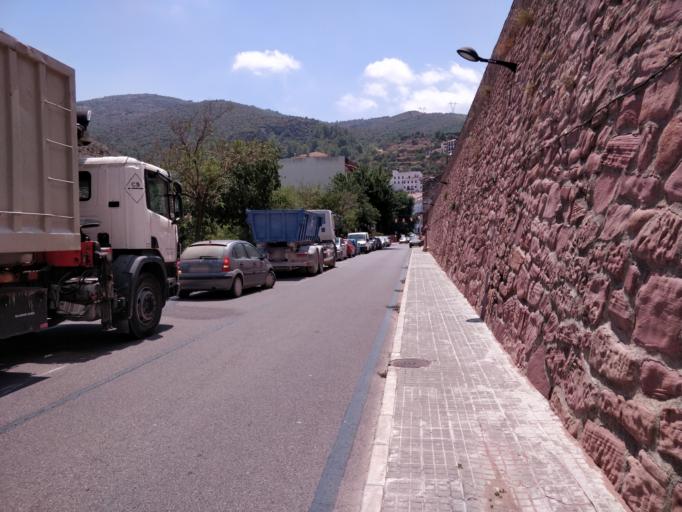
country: ES
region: Valencia
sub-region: Provincia de Castello
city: Villafames
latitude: 40.1142
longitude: -0.0530
